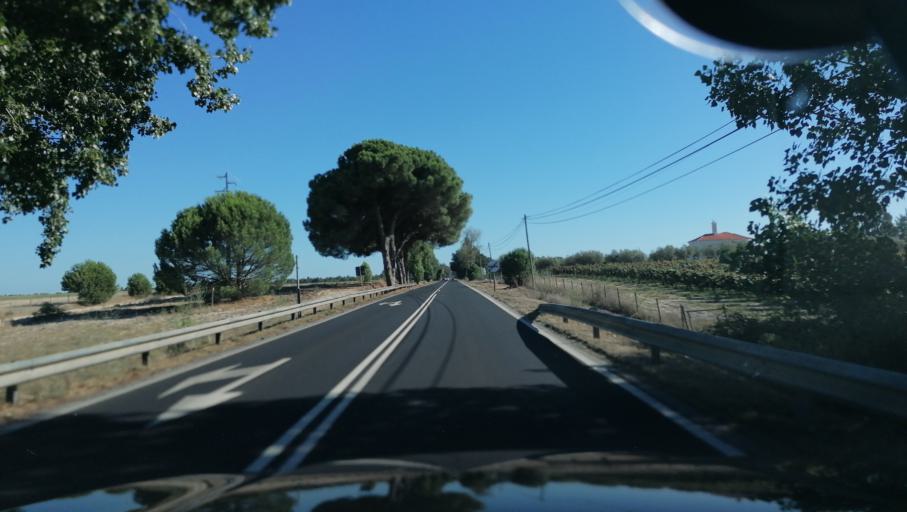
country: PT
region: Santarem
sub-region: Benavente
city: Poceirao
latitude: 38.8123
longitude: -8.8808
